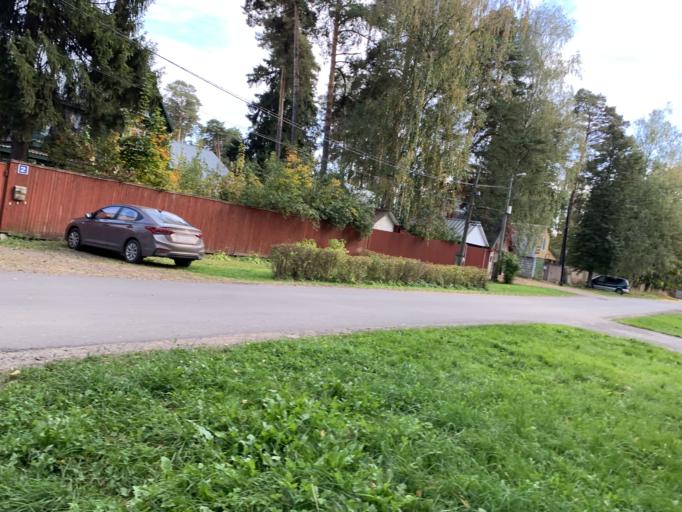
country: RU
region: Moskovskaya
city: Mamontovka
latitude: 55.9806
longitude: 37.8314
